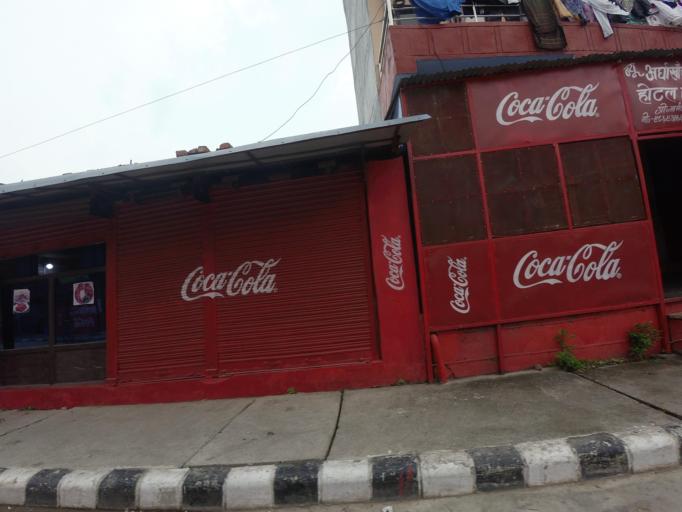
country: NP
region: Western Region
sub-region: Lumbini Zone
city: Bhairahawa
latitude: 27.4898
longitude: 83.4497
